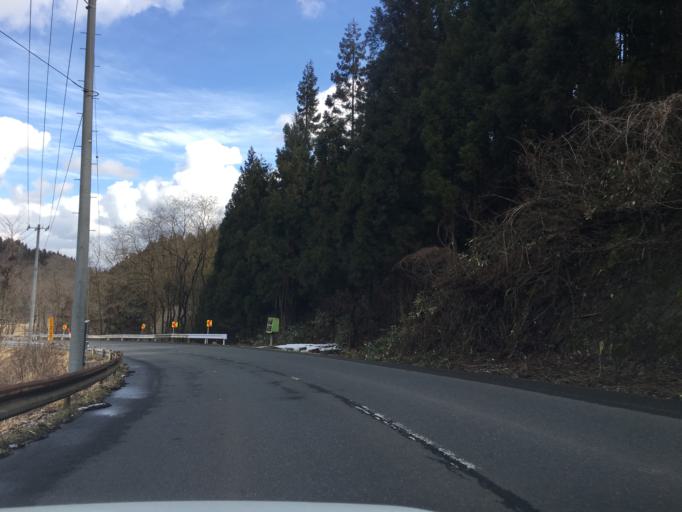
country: JP
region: Akita
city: Odate
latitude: 40.1921
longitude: 140.5262
